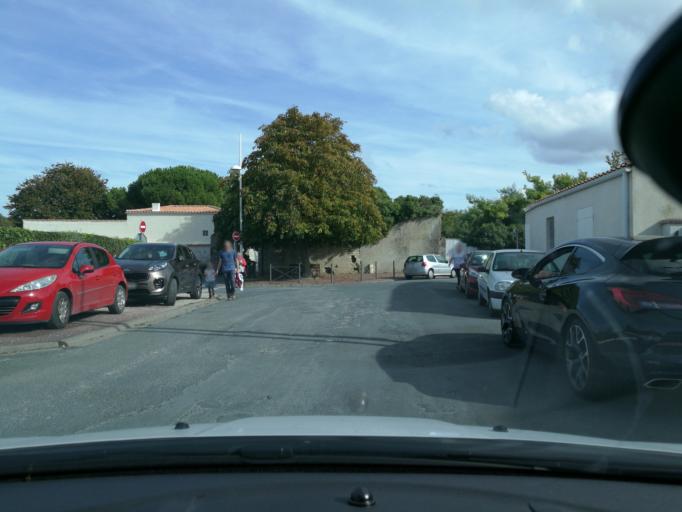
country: FR
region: Poitou-Charentes
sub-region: Departement de la Charente-Maritime
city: Dolus-d'Oleron
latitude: 45.9445
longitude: -1.3086
